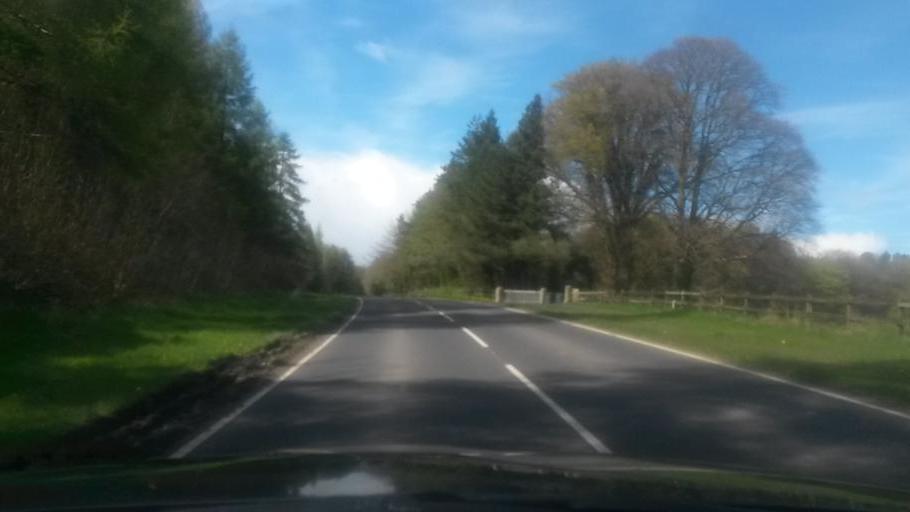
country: GB
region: Northern Ireland
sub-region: Fermanagh District
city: Enniskillen
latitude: 54.3791
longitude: -7.6886
